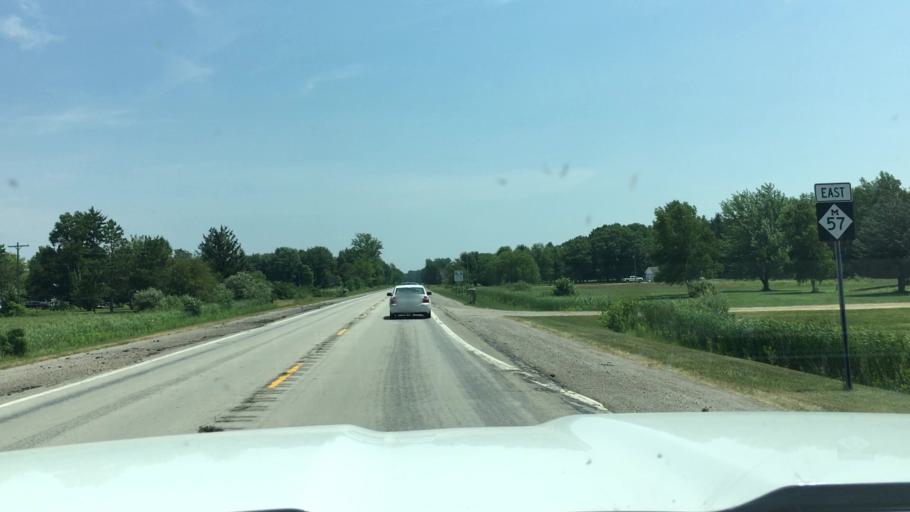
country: US
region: Michigan
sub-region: Shiawassee County
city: New Haven
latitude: 43.1867
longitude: -84.3060
